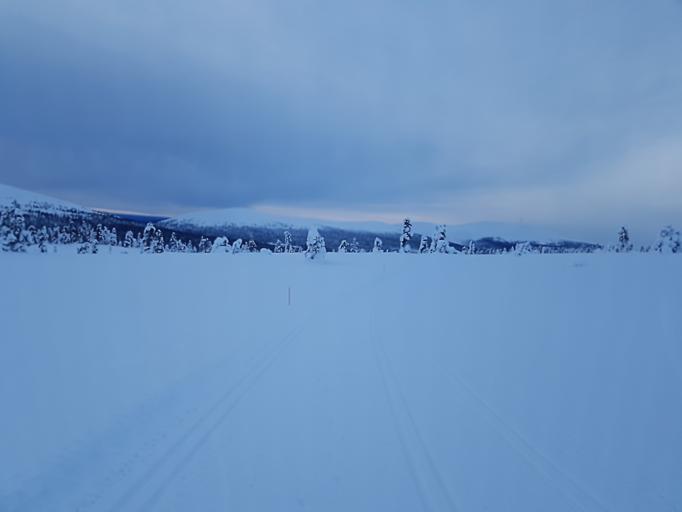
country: FI
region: Lapland
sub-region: Tunturi-Lappi
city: Kolari
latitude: 67.6577
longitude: 24.2287
